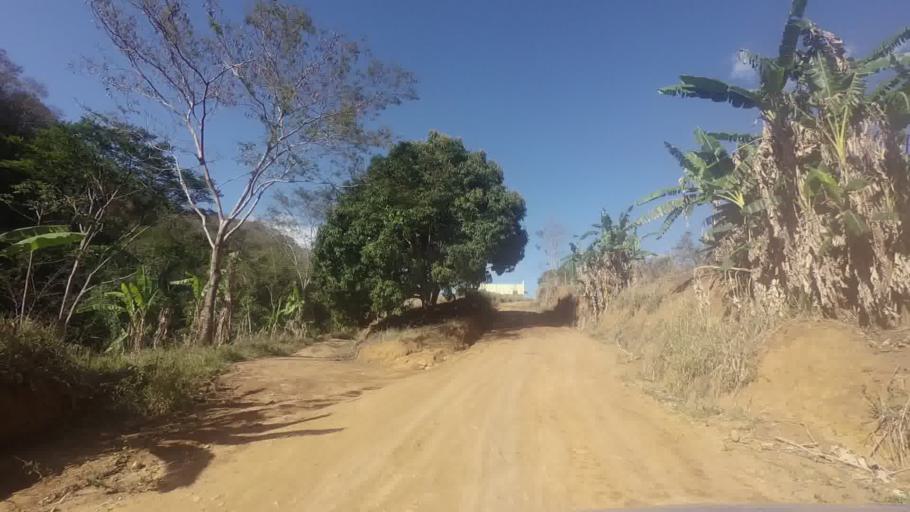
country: BR
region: Espirito Santo
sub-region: Sao Jose Do Calcado
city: Sao Jose do Calcado
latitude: -21.0308
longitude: -41.5904
